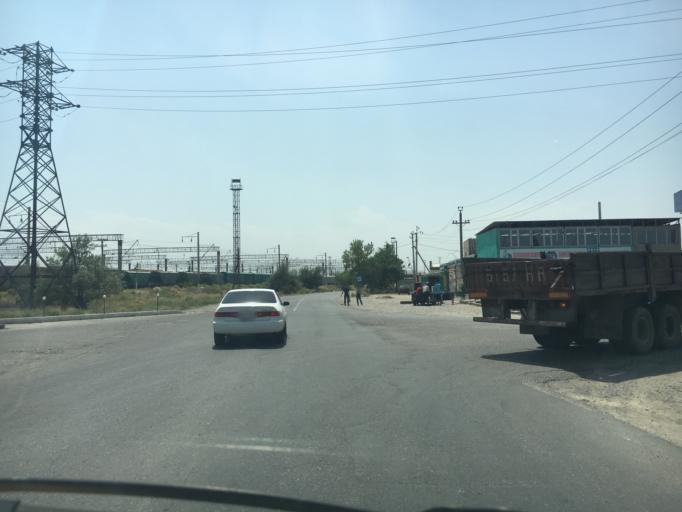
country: KZ
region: Zhambyl
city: Taraz
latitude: 42.8613
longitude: 71.3585
